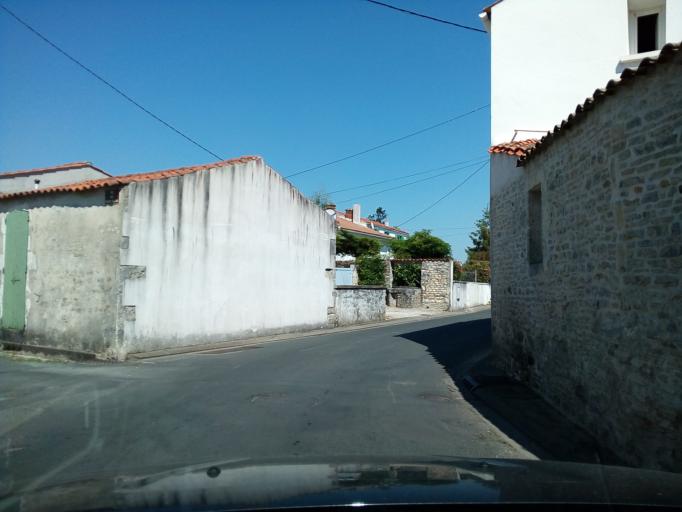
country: FR
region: Poitou-Charentes
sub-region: Departement de la Charente-Maritime
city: Boyard-Ville
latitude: 45.9711
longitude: -1.2946
